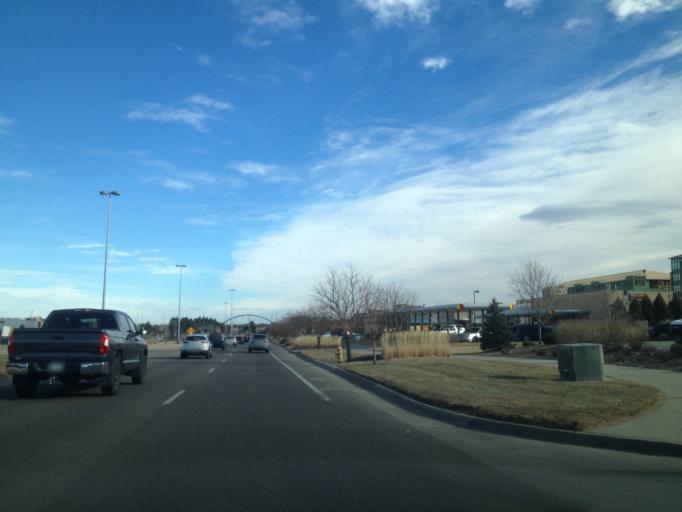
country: US
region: Colorado
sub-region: Boulder County
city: Superior
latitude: 39.9287
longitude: -105.1411
